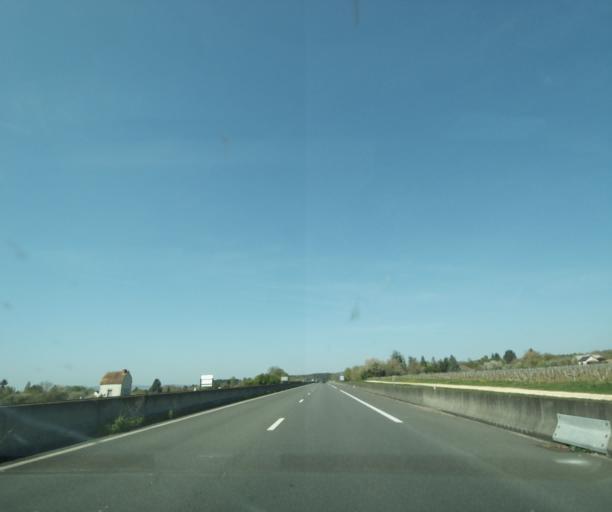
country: FR
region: Bourgogne
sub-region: Departement de la Nievre
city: Pouilly-sur-Loire
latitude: 47.2835
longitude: 2.9685
